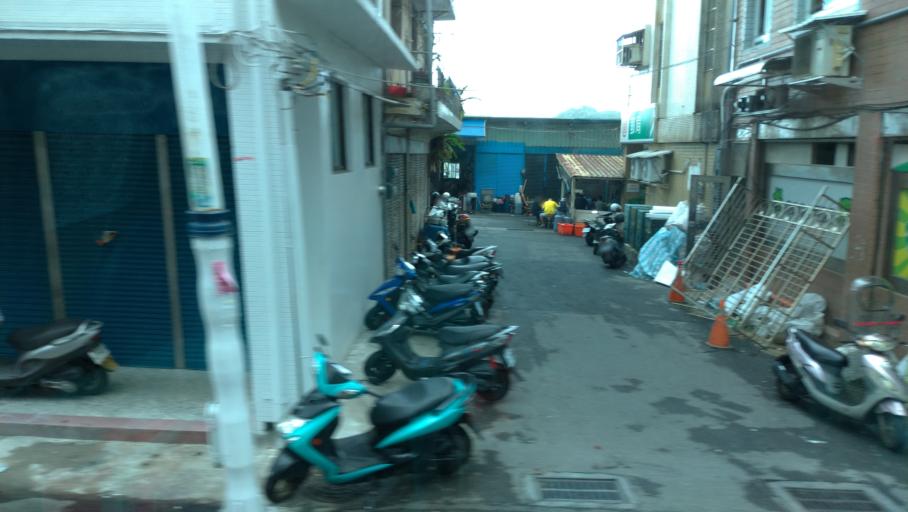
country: TW
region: Taiwan
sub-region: Keelung
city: Keelung
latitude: 25.1509
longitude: 121.7664
